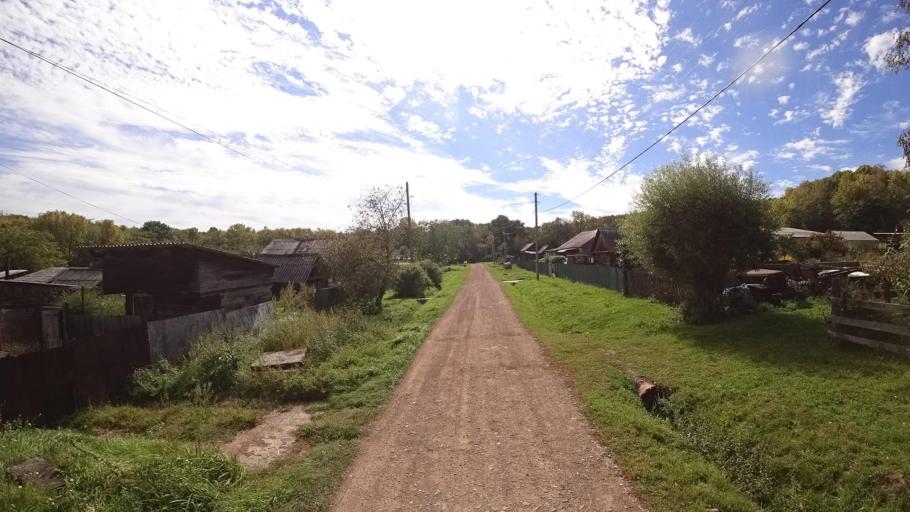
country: RU
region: Primorskiy
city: Yakovlevka
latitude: 44.3944
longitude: 133.5966
